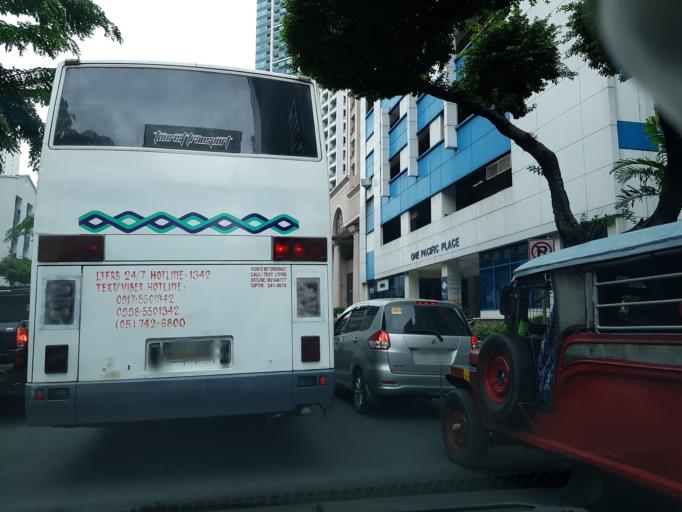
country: PH
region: Metro Manila
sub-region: Makati City
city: Makati City
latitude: 14.5622
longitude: 121.0187
